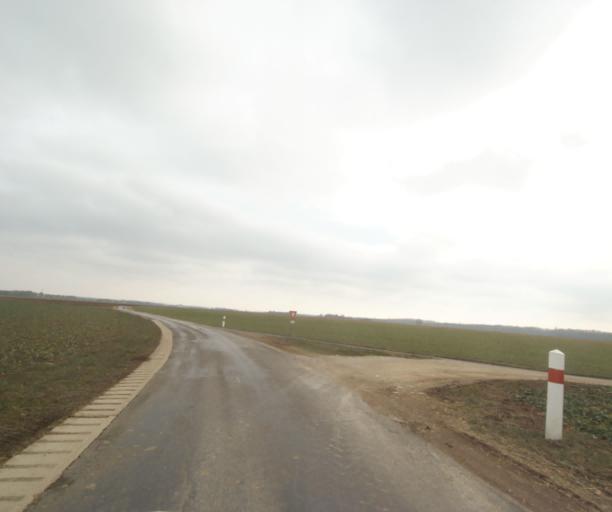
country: FR
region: Champagne-Ardenne
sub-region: Departement de la Haute-Marne
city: Villiers-en-Lieu
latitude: 48.6809
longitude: 4.8451
